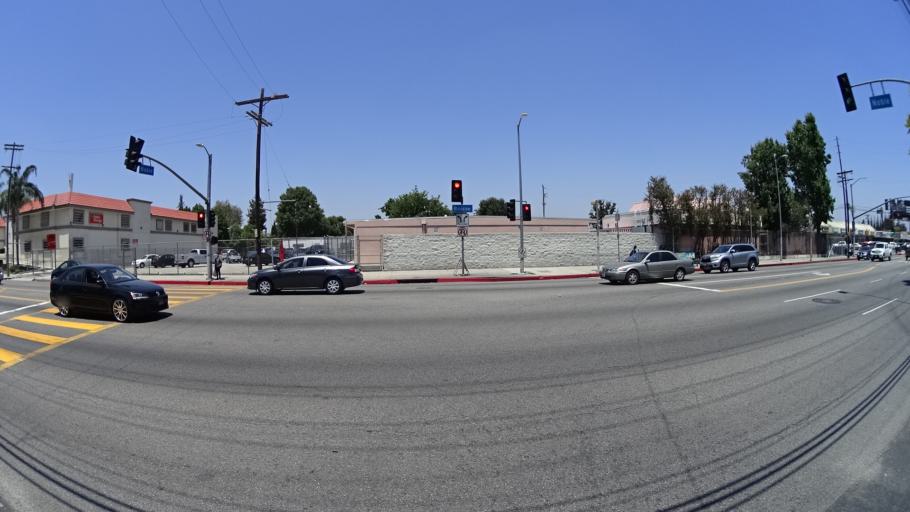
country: US
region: California
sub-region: Los Angeles County
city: Van Nuys
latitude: 34.2214
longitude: -118.4619
